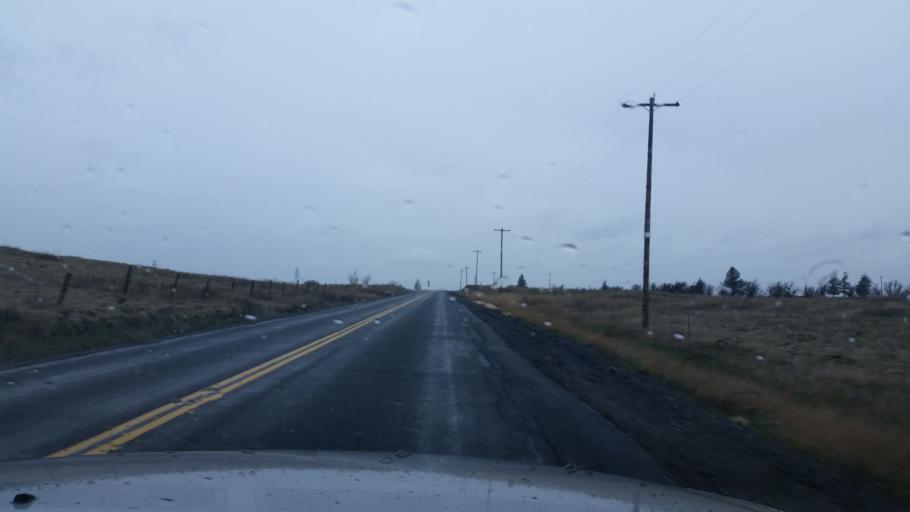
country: US
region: Washington
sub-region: Spokane County
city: Airway Heights
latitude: 47.6864
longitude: -117.5653
